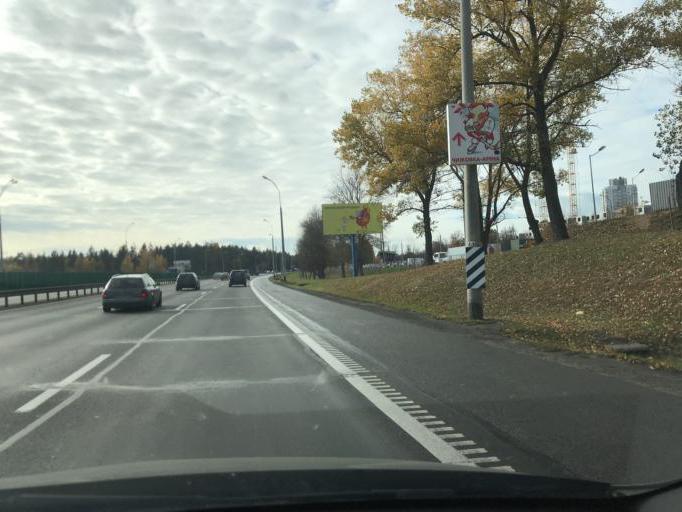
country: BY
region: Minsk
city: Hatava
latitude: 53.8363
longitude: 27.6546
